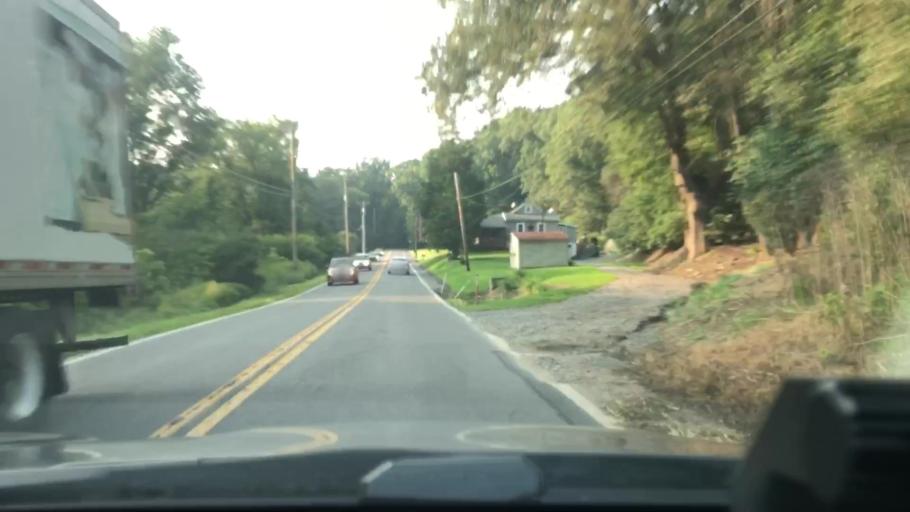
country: US
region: Pennsylvania
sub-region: Berks County
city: Kutztown
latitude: 40.5612
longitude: -75.8085
